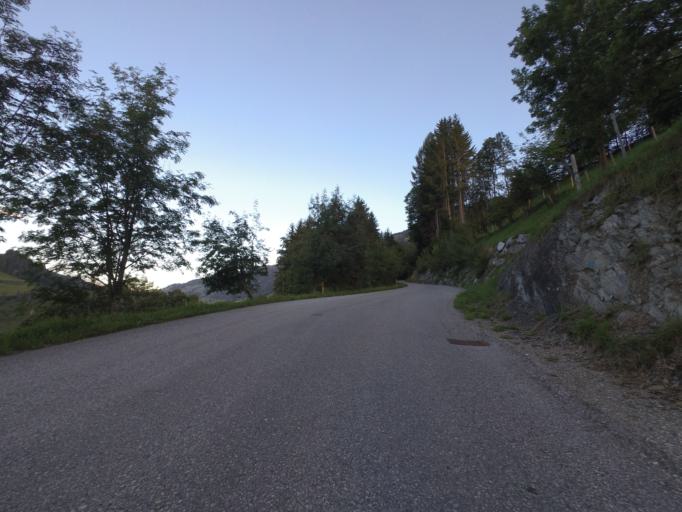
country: AT
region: Salzburg
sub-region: Politischer Bezirk Sankt Johann im Pongau
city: Goldegg
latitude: 47.3356
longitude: 13.1129
